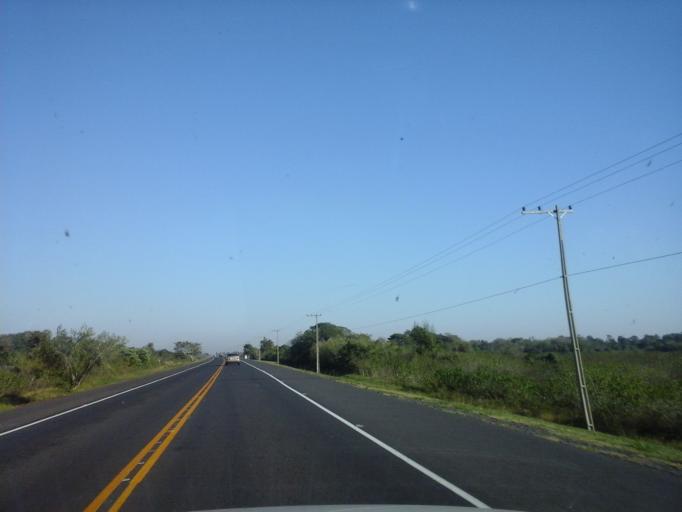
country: PY
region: Neembucu
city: Pilar
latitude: -26.8548
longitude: -58.2001
